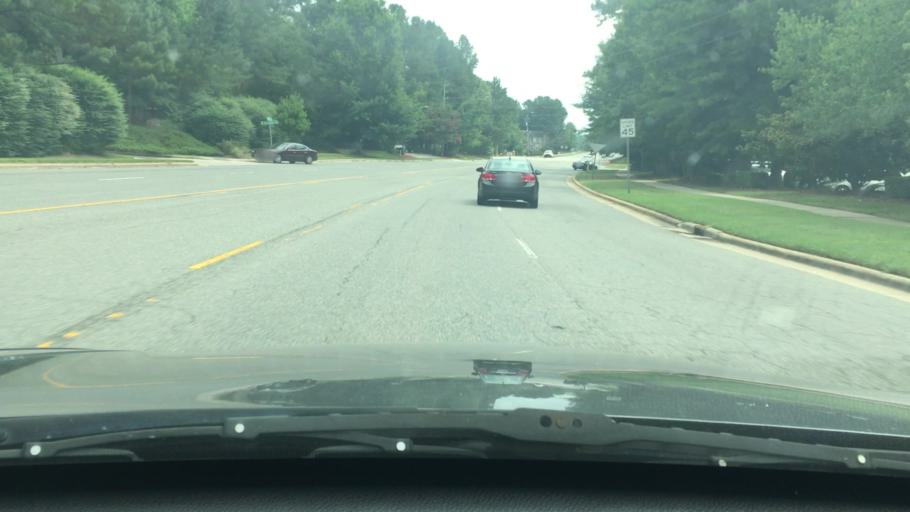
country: US
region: North Carolina
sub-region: Wake County
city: West Raleigh
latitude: 35.8548
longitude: -78.7116
